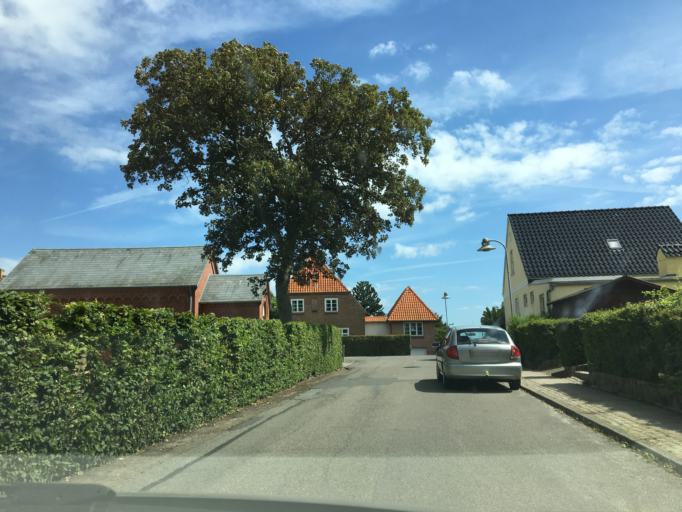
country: DK
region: South Denmark
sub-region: Langeland Kommune
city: Rudkobing
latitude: 54.9341
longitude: 10.7067
